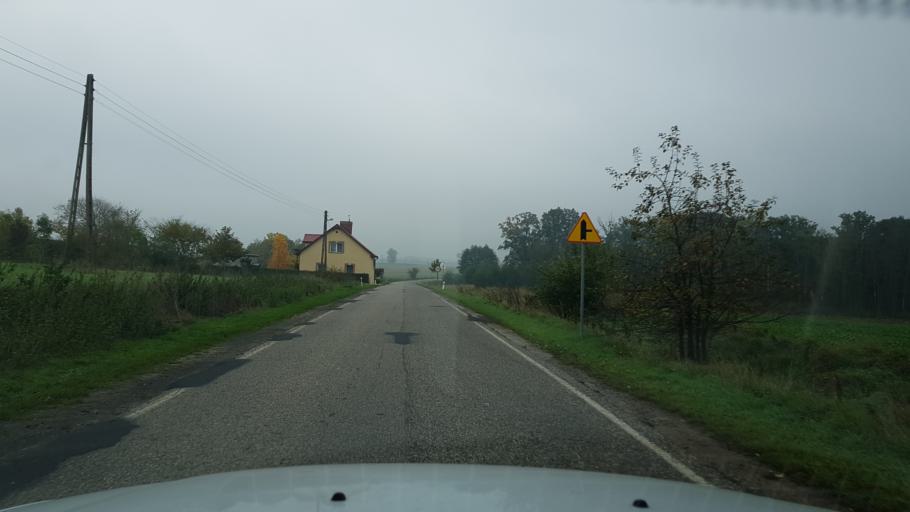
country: PL
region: West Pomeranian Voivodeship
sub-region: Powiat stargardzki
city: Dolice
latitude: 53.1581
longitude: 15.2376
